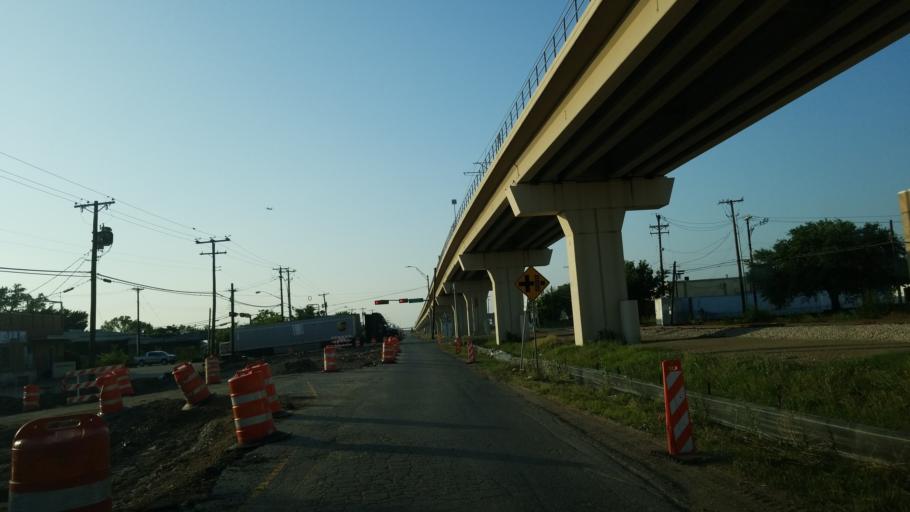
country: US
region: Texas
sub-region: Dallas County
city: Farmers Branch
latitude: 32.8857
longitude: -96.8852
